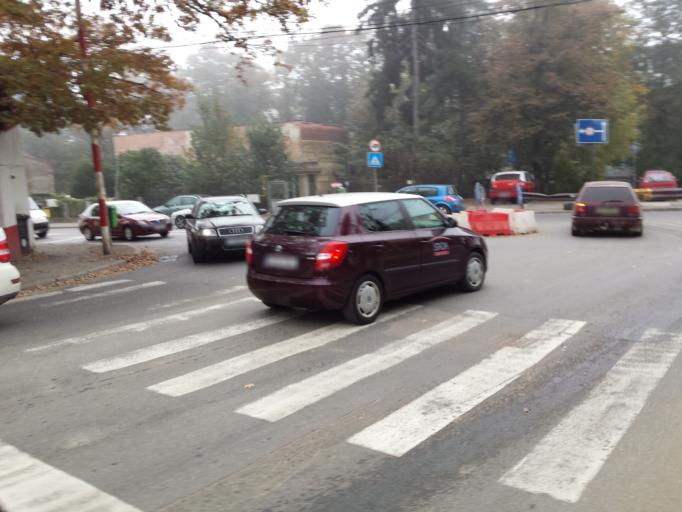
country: RO
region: Cluj
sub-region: Municipiul Cluj-Napoca
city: Cluj-Napoca
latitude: 46.7732
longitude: 23.5615
